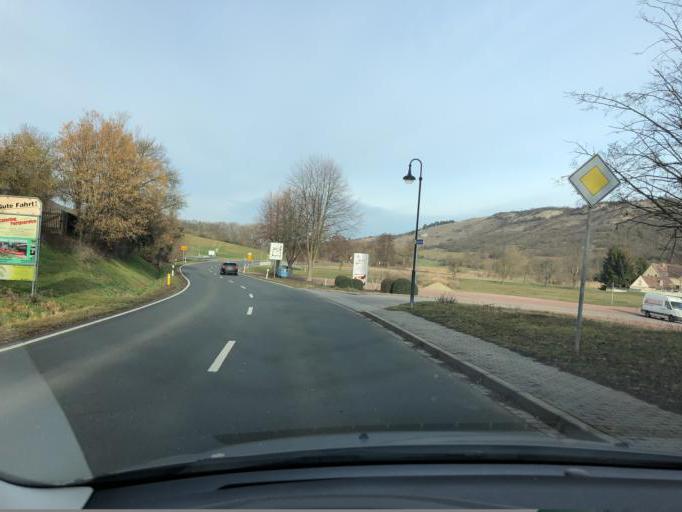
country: DE
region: Saxony-Anhalt
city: Balgstadt
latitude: 51.2070
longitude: 11.7295
